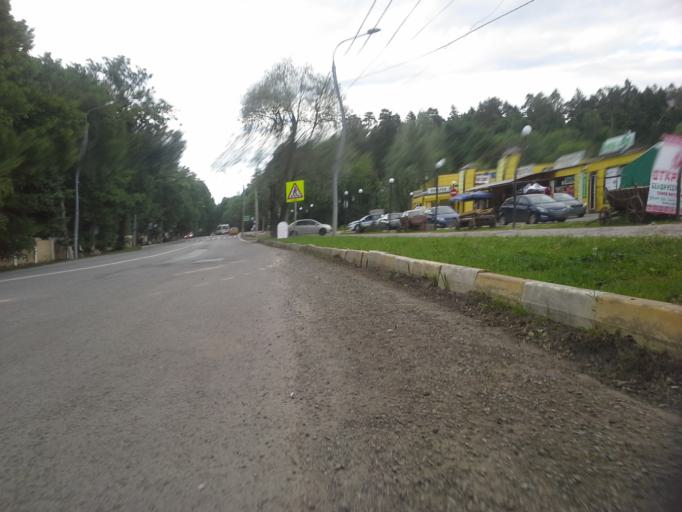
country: RU
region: Moskovskaya
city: Filimonki
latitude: 55.5717
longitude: 37.3581
